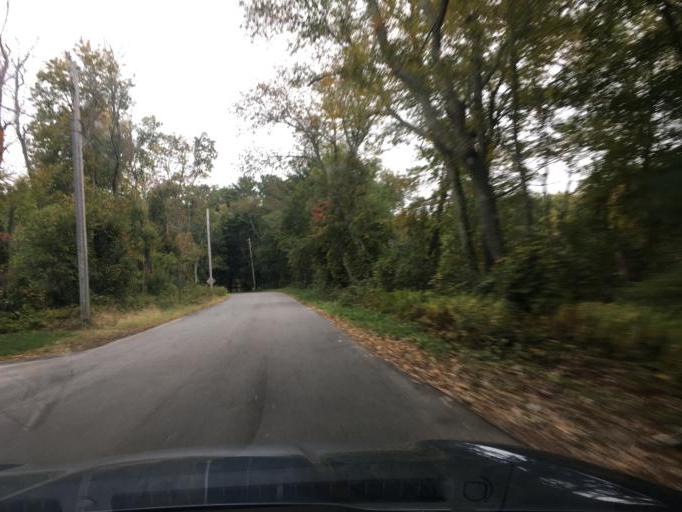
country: US
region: Rhode Island
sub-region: Washington County
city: Exeter
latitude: 41.6049
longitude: -71.5691
